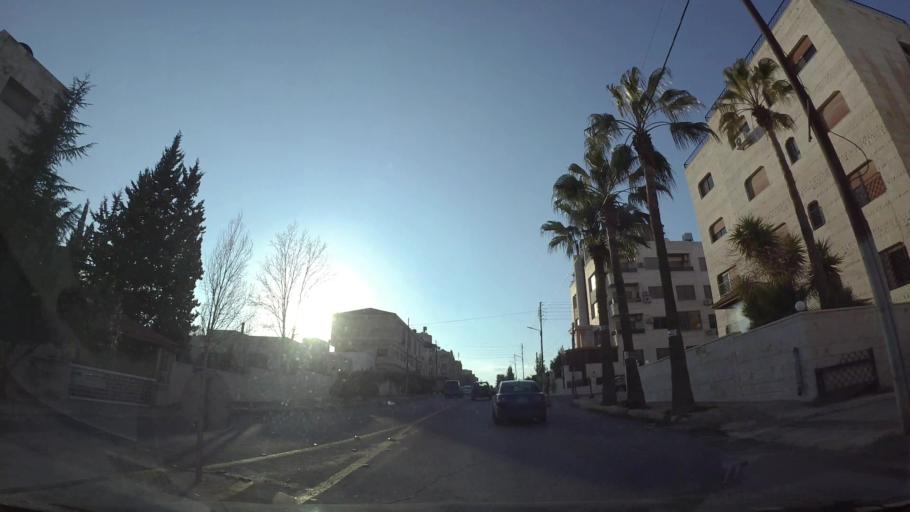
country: JO
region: Amman
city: Al Jubayhah
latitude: 31.9738
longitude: 35.8791
